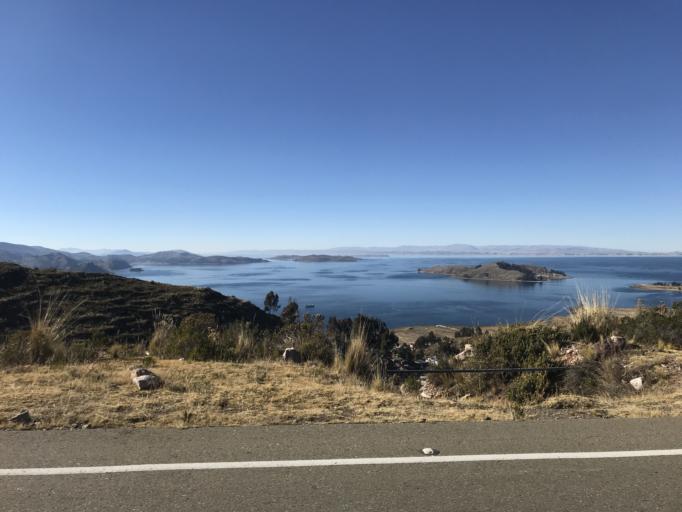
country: BO
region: La Paz
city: San Pedro
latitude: -16.1876
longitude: -68.9669
